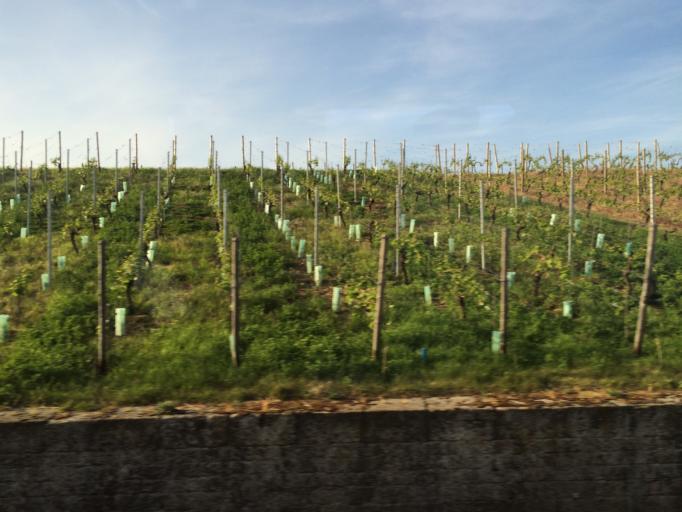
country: DE
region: Hesse
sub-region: Regierungsbezirk Darmstadt
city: Bischofsheim
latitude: 50.0037
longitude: 8.3664
